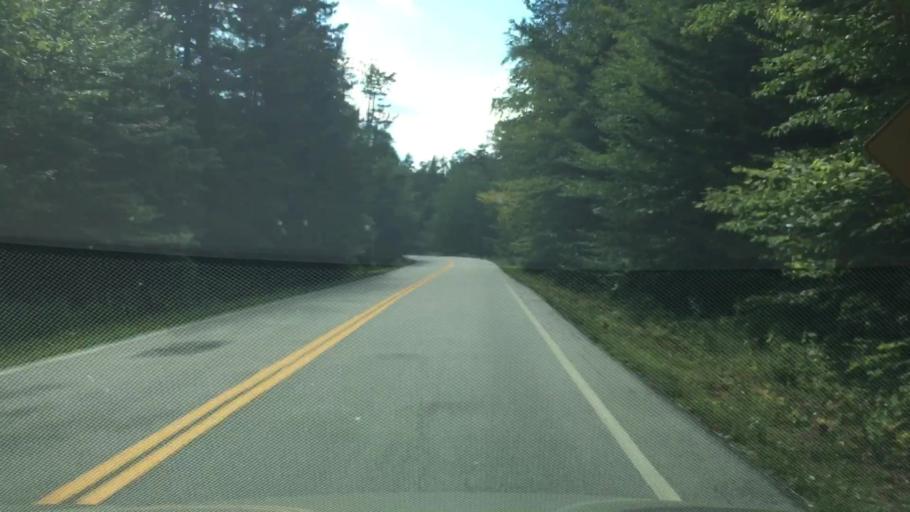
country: US
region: New Hampshire
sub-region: Carroll County
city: North Conway
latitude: 44.0436
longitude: -71.3143
